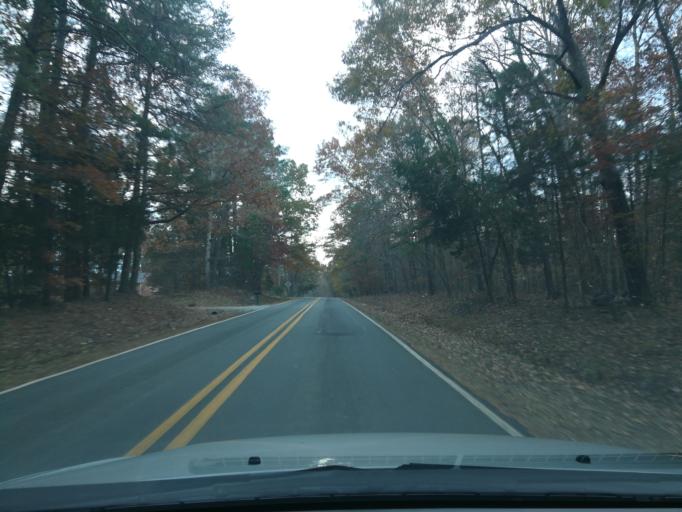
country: US
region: North Carolina
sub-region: Orange County
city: Hillsborough
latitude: 36.0319
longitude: -79.0385
